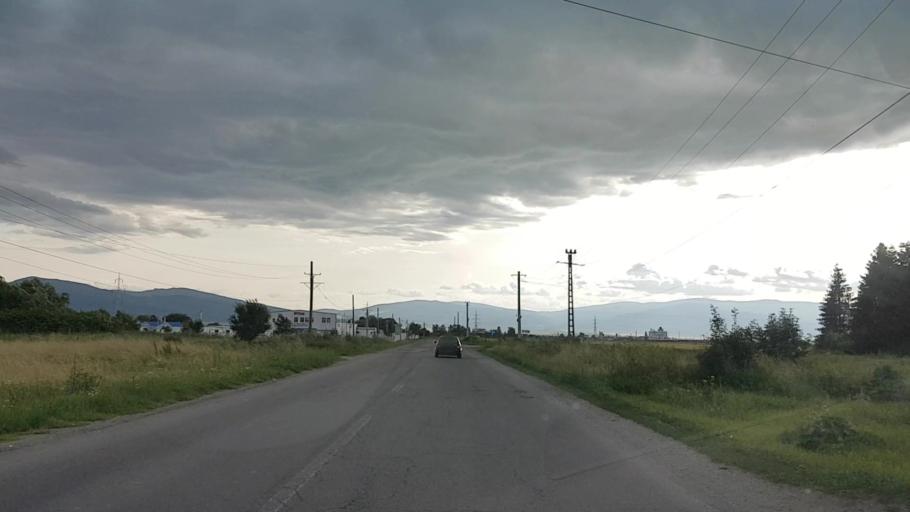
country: RO
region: Harghita
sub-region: Municipiul Gheorgheni
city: Gheorgheni
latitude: 46.7126
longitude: 25.5620
